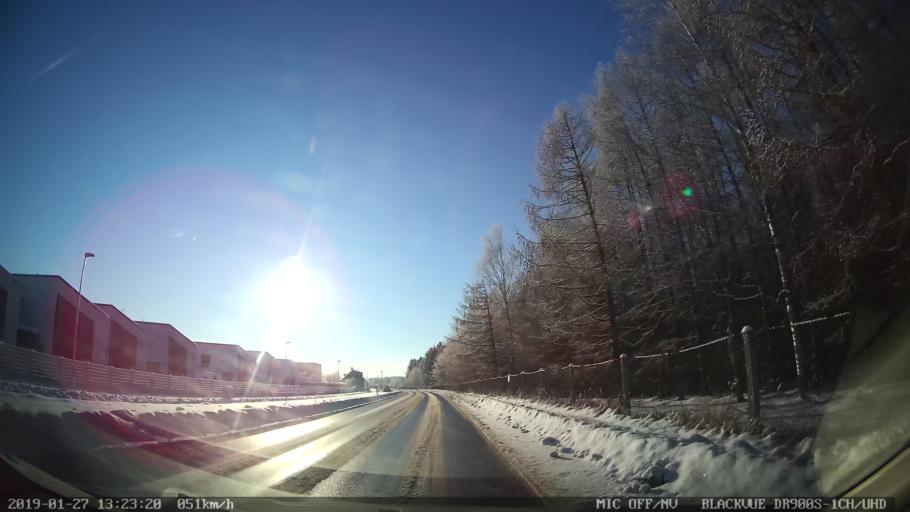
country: EE
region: Harju
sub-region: Tallinna linn
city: Tallinn
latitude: 59.4071
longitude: 24.7954
